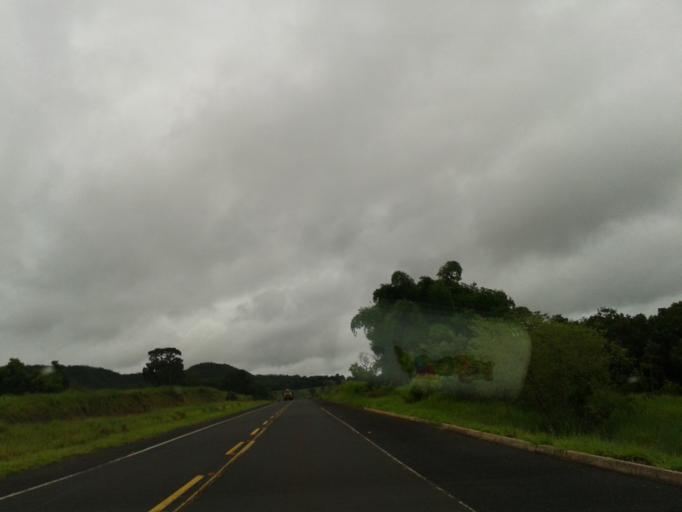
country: BR
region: Minas Gerais
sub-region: Santa Vitoria
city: Santa Vitoria
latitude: -19.2044
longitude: -50.0258
